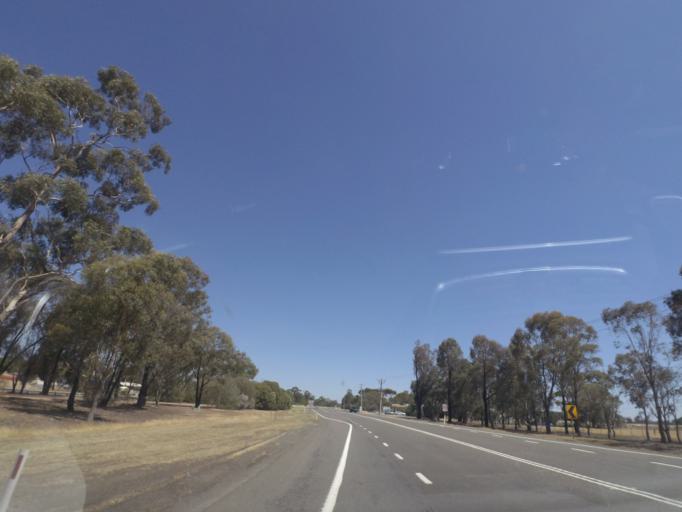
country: AU
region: Victoria
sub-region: Greater Shepparton
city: Shepparton
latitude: -36.2373
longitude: 145.4314
